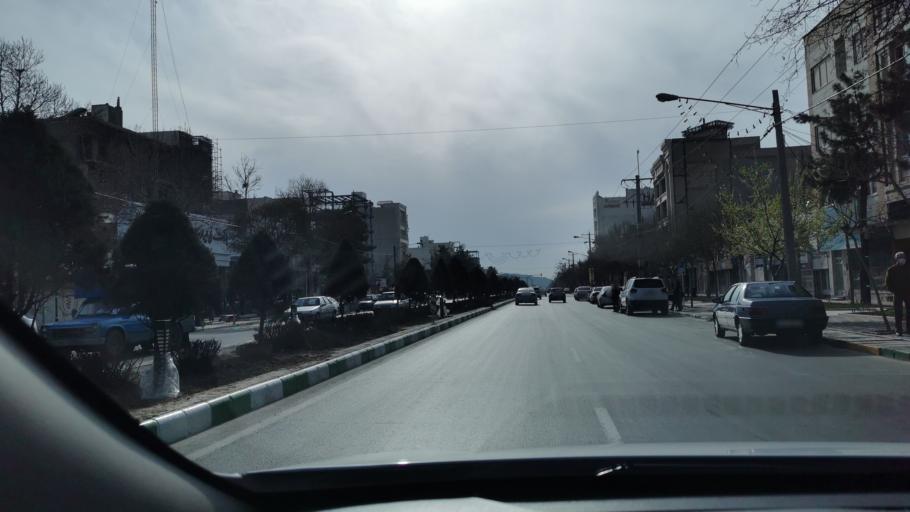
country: IR
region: Razavi Khorasan
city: Mashhad
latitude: 36.2907
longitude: 59.5384
